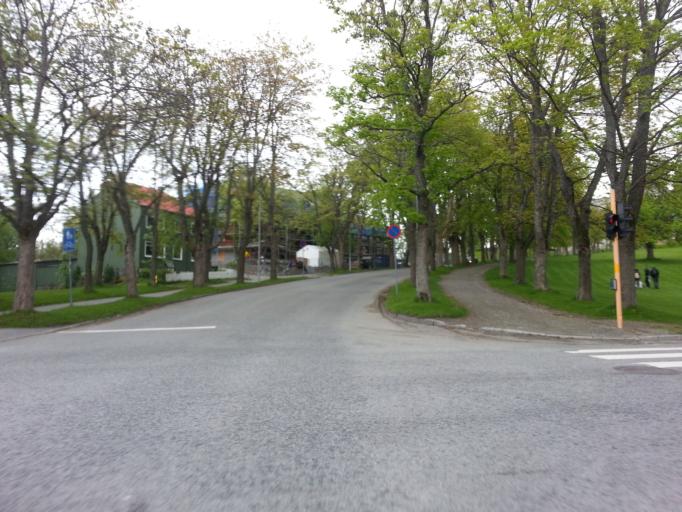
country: NO
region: Sor-Trondelag
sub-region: Trondheim
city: Trondheim
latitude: 63.4215
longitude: 10.3987
